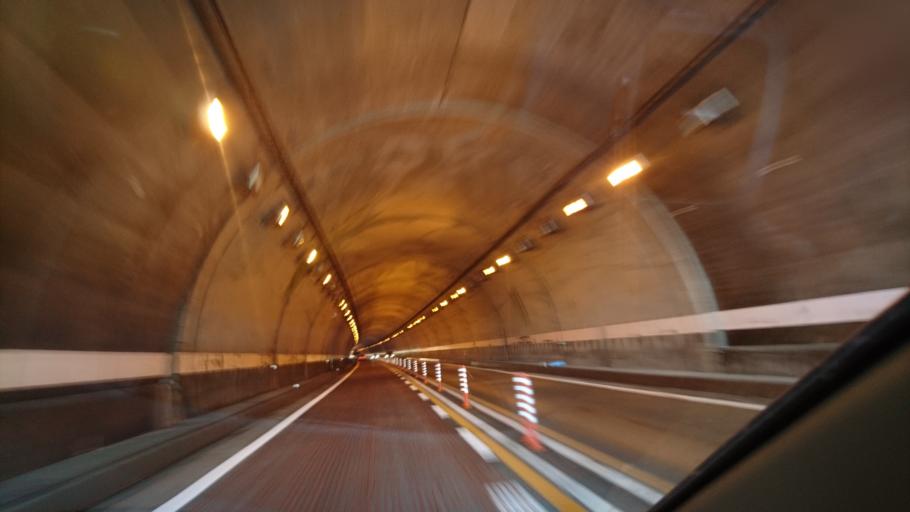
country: JP
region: Akita
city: Yokotemachi
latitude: 39.3152
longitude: 140.7660
